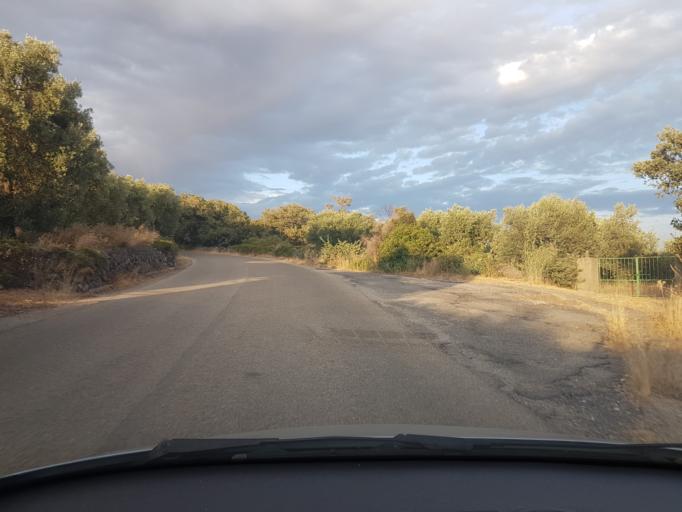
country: IT
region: Sardinia
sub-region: Provincia di Oristano
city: Seneghe
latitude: 40.0952
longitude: 8.6265
